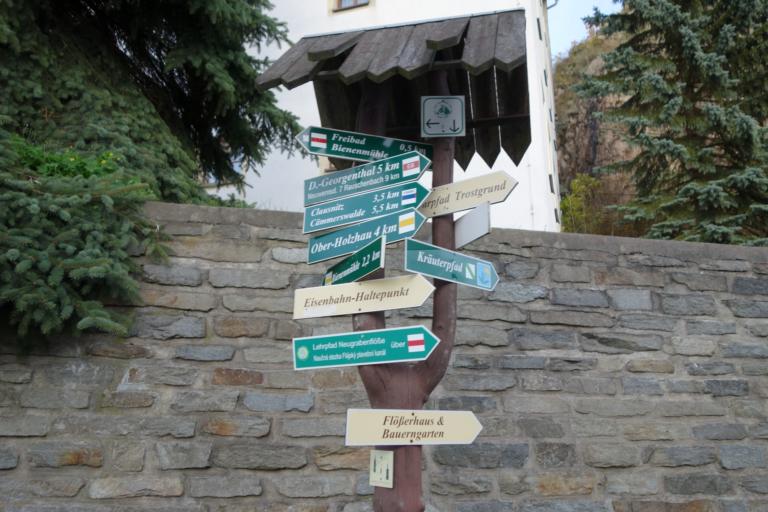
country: DE
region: Saxony
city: Rechenberg-Bienenmuhle
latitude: 50.7360
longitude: 13.5558
